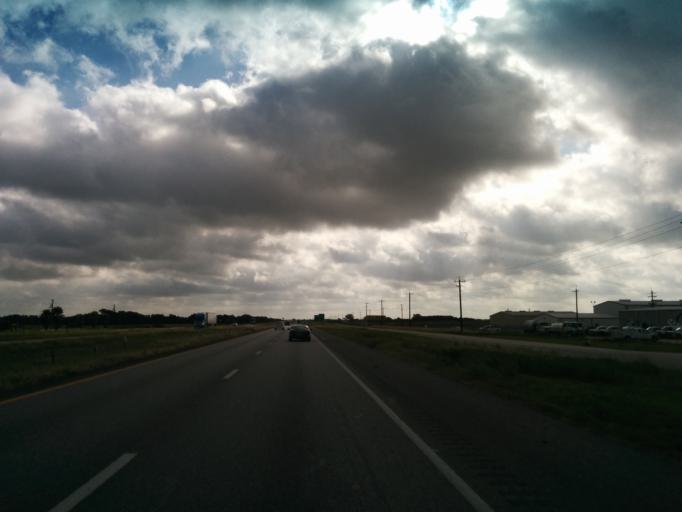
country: US
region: Texas
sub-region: Guadalupe County
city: Marion
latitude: 29.5114
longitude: -98.1588
